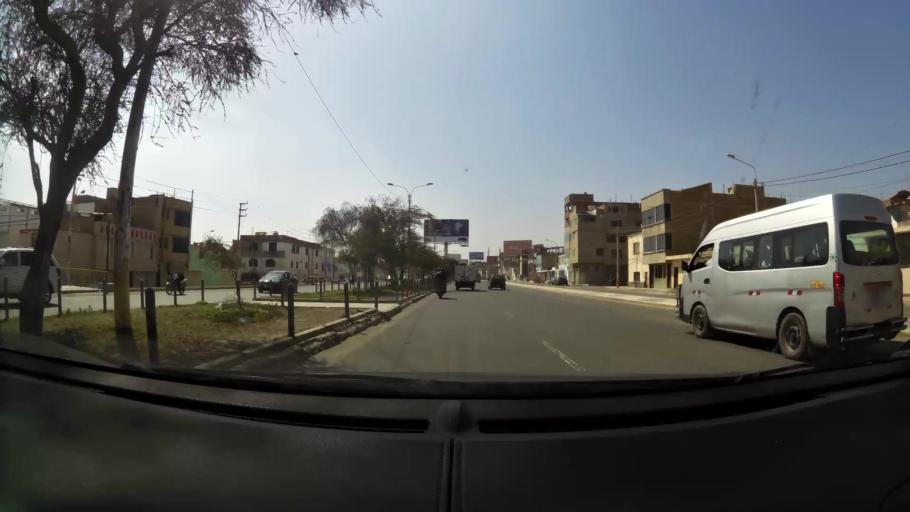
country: PE
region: Lambayeque
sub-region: Provincia de Chiclayo
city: Chiclayo
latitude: -6.7827
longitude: -79.8336
